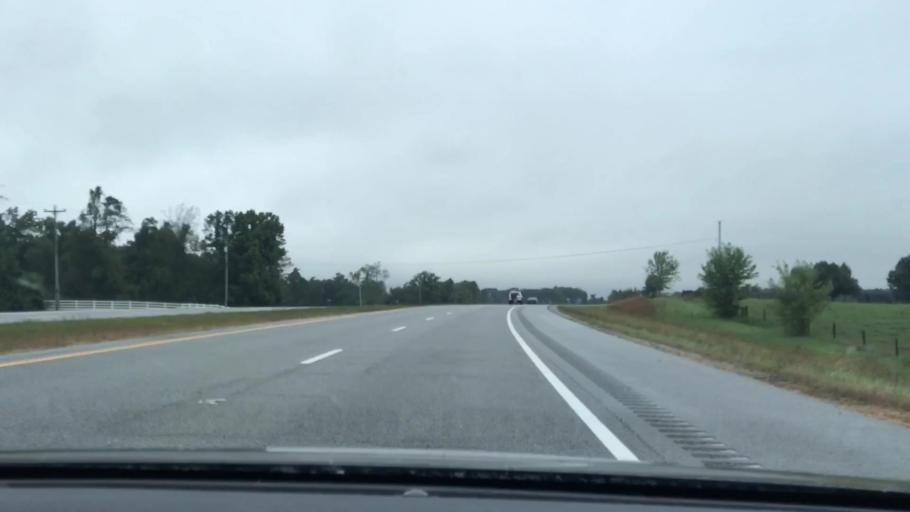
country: US
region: Tennessee
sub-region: Fentress County
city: Grimsley
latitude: 36.3108
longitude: -84.9735
